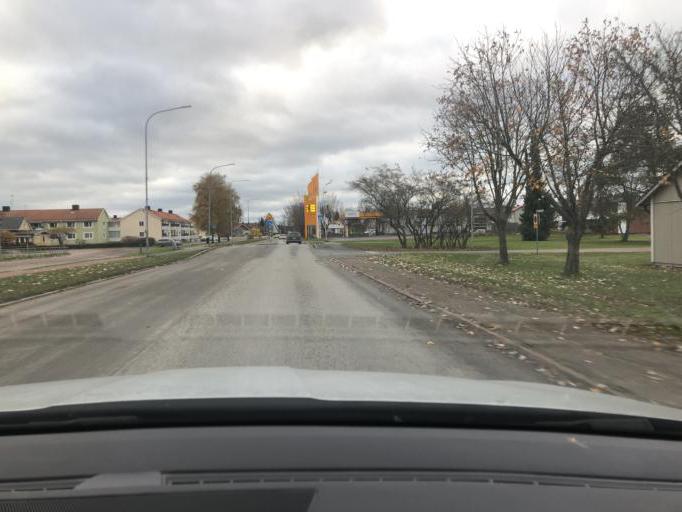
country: SE
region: Uppsala
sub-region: Tierps Kommun
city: Tierp
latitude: 60.3451
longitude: 17.5052
